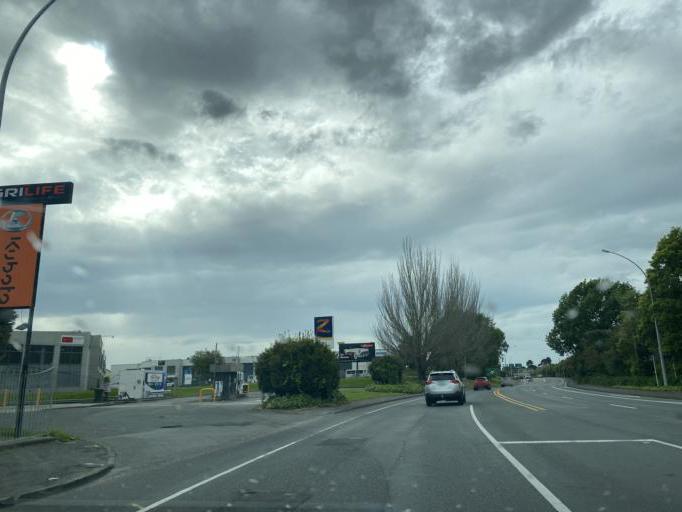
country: NZ
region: Waikato
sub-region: Hamilton City
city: Hamilton
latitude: -37.7858
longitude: 175.2557
